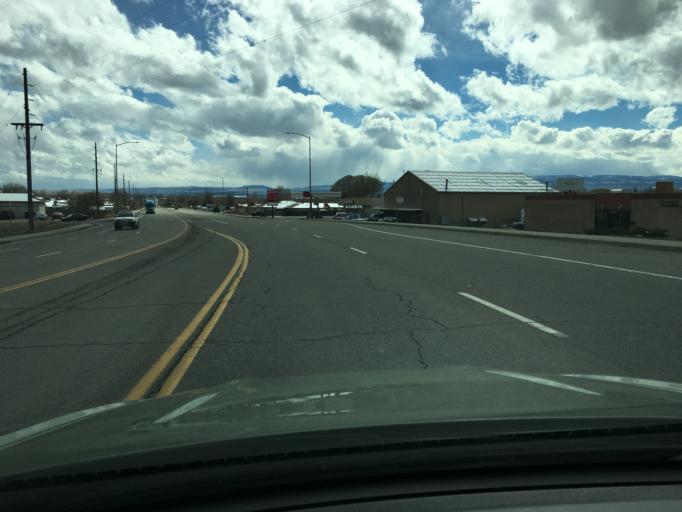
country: US
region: Colorado
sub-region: Mesa County
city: Clifton
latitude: 39.0836
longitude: -108.4594
